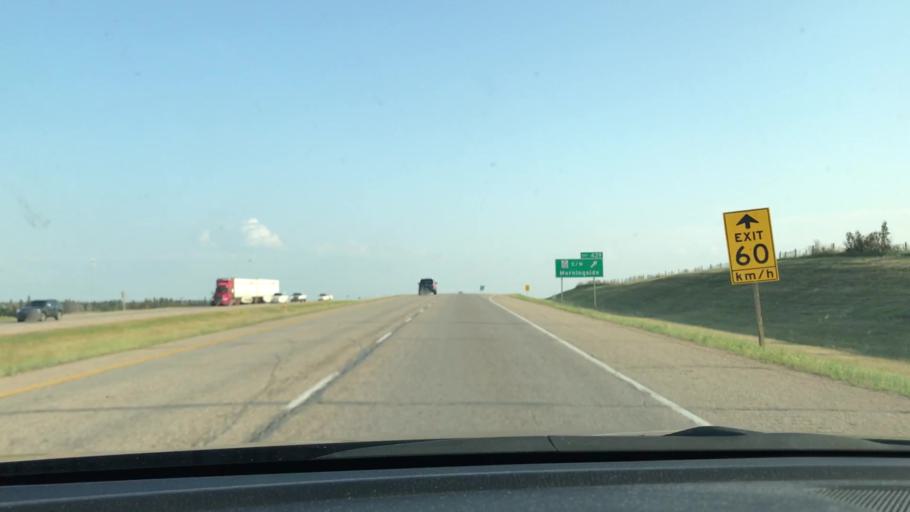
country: CA
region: Alberta
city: Ponoka
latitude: 52.5843
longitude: -113.6633
